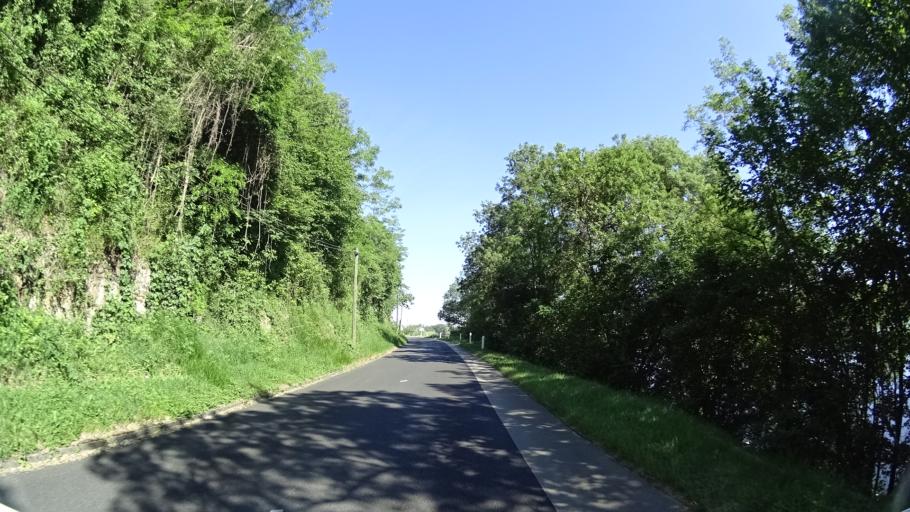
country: FR
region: Pays de la Loire
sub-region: Departement de Maine-et-Loire
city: Saint-Martin-de-la-Place
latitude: 47.3036
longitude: -0.1458
